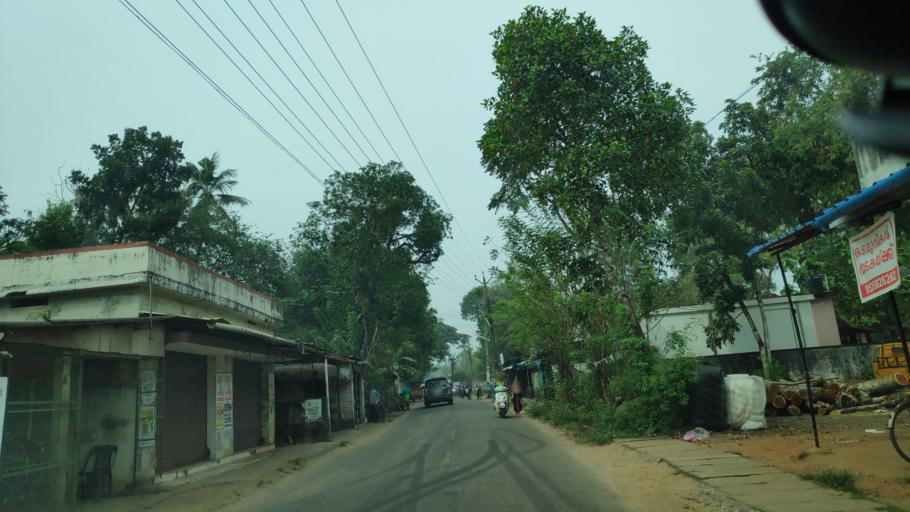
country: IN
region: Kerala
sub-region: Alappuzha
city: Alleppey
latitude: 9.5723
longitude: 76.3435
